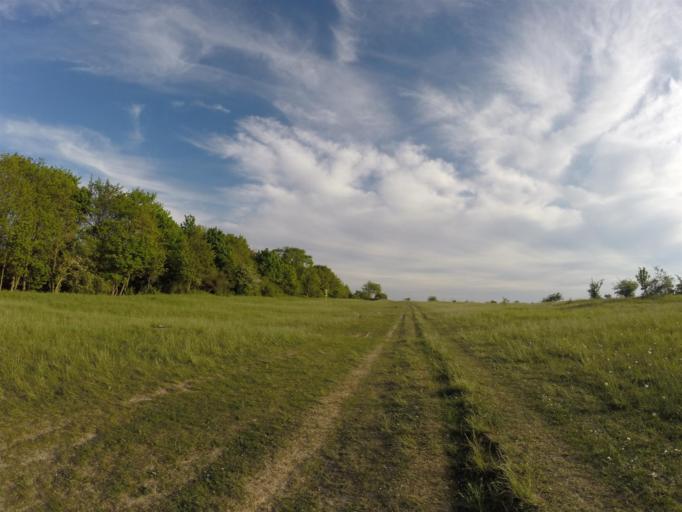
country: DE
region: Thuringia
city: Jena
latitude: 50.9476
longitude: 11.5739
